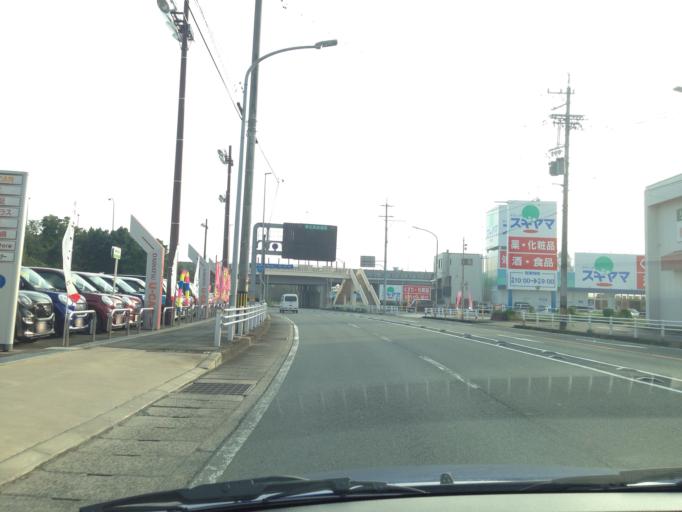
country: JP
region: Aichi
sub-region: Tokai-shi
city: Toyokawa
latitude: 34.8399
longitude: 137.4113
